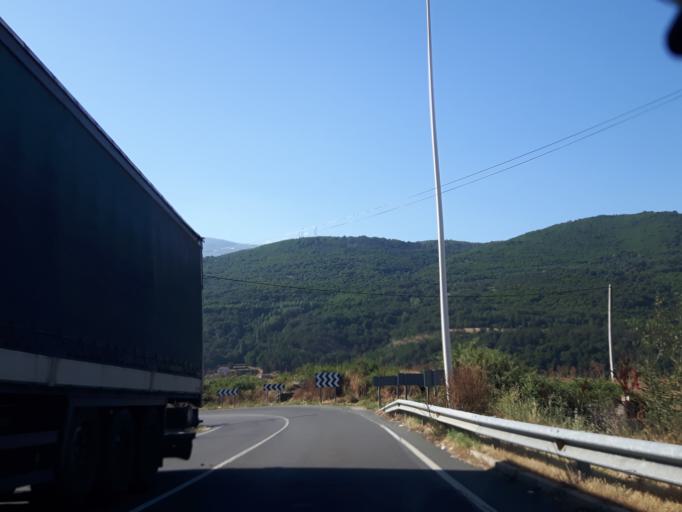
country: ES
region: Castille and Leon
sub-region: Provincia de Salamanca
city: Bejar
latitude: 40.3922
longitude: -5.7824
